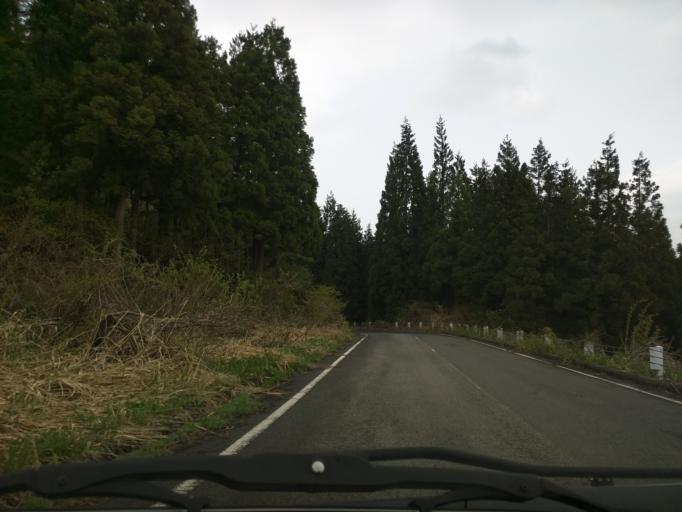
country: JP
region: Fukushima
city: Kitakata
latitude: 37.4198
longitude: 139.7721
